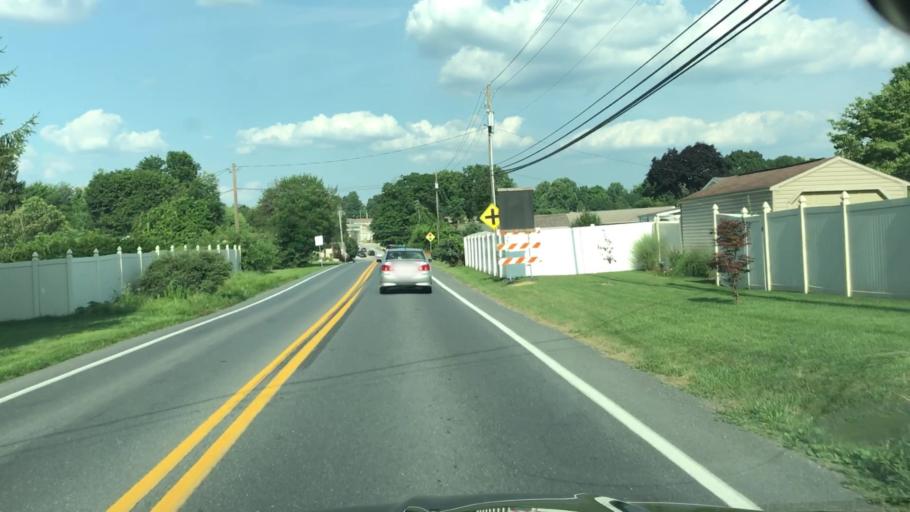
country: US
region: Pennsylvania
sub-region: Cumberland County
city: Mechanicsburg
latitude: 40.1623
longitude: -77.0068
